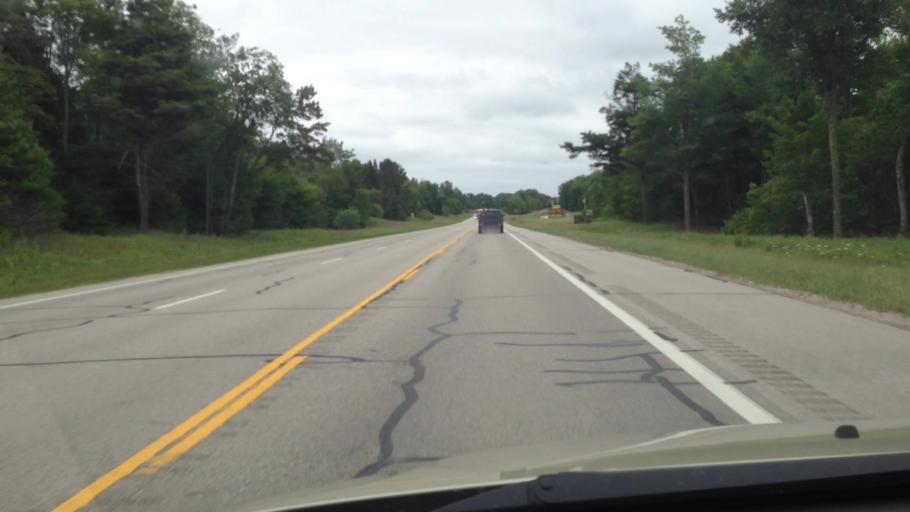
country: US
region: Michigan
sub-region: Mackinac County
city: Saint Ignace
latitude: 46.0137
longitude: -85.0151
